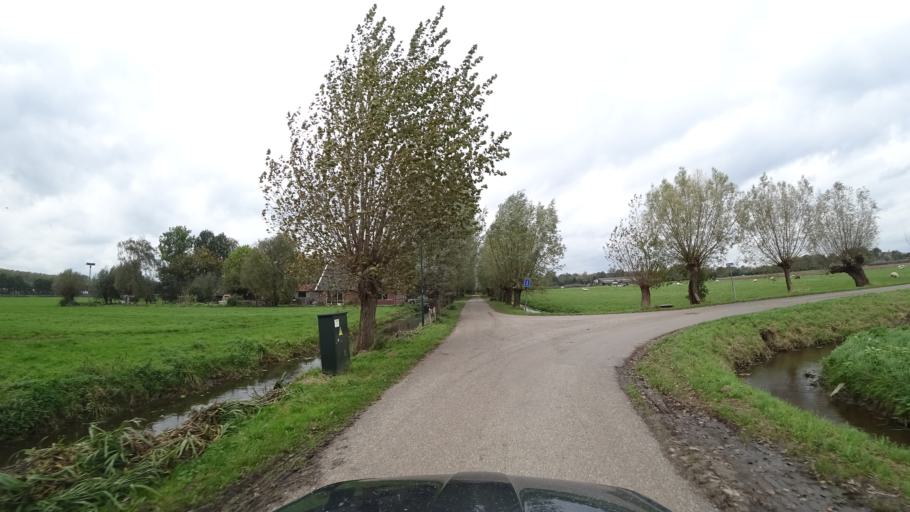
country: NL
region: Utrecht
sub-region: Stichtse Vecht
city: Spechtenkamp
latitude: 52.1545
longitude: 5.0101
